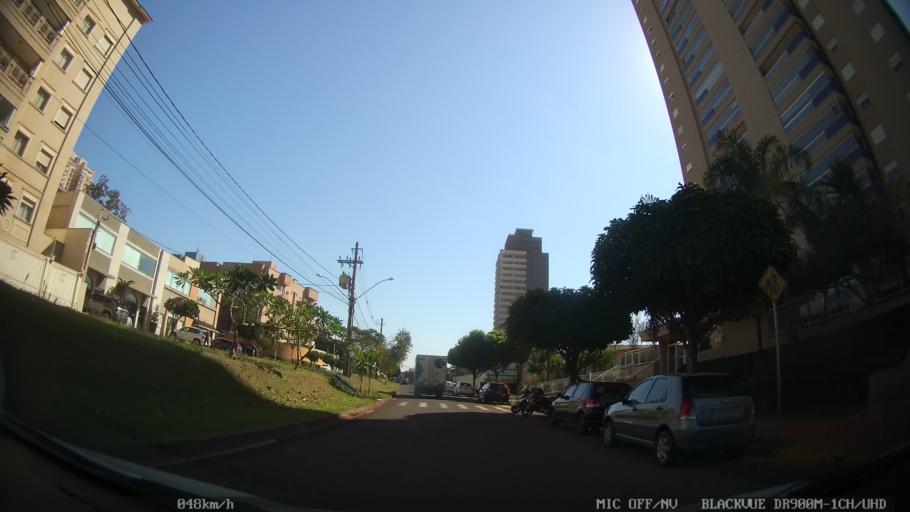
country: BR
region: Sao Paulo
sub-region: Ribeirao Preto
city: Ribeirao Preto
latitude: -21.2122
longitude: -47.8016
